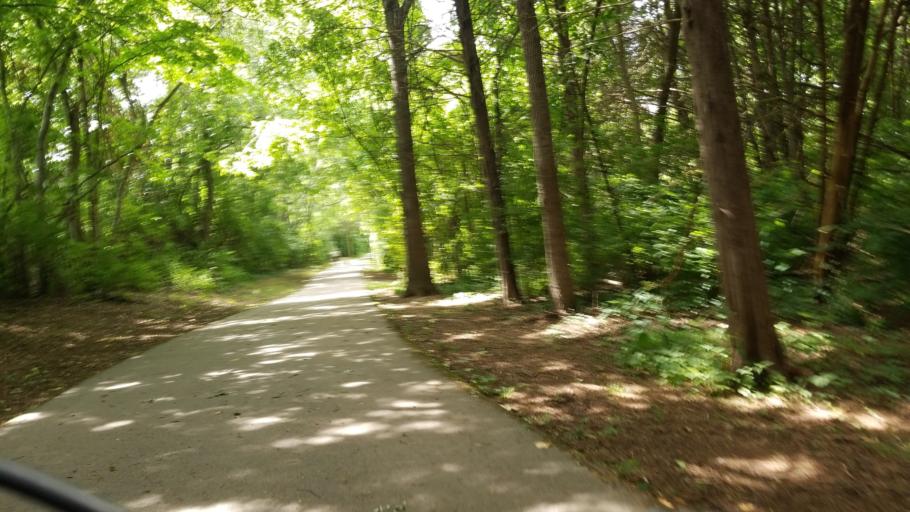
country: US
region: Tennessee
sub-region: Davidson County
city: Forest Hills
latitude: 36.0345
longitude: -86.8371
